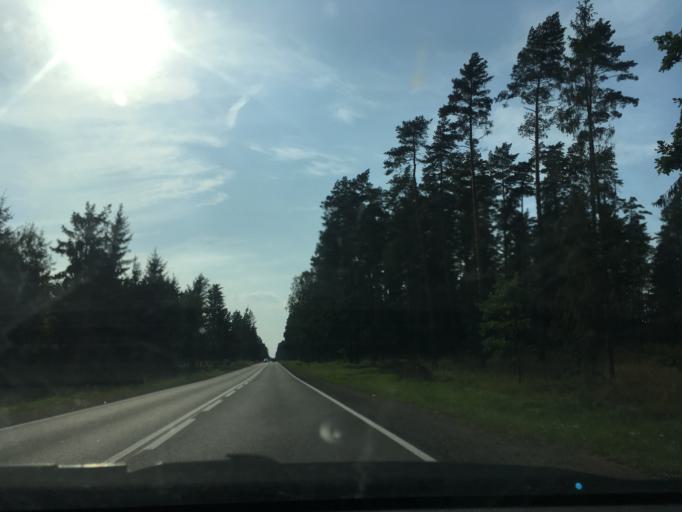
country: PL
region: Podlasie
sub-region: Powiat bialostocki
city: Suprasl
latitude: 53.1256
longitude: 23.3617
